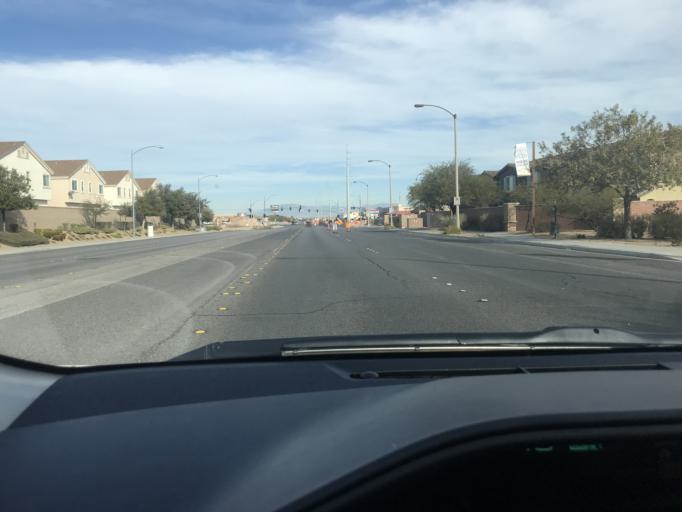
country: US
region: Nevada
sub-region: Clark County
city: Enterprise
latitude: 36.0181
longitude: -115.2794
